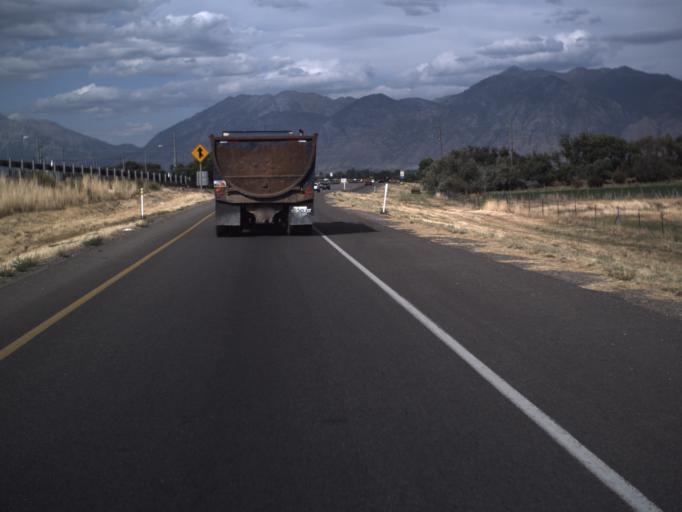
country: US
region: Utah
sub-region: Utah County
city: Payson
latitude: 40.0563
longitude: -111.7308
